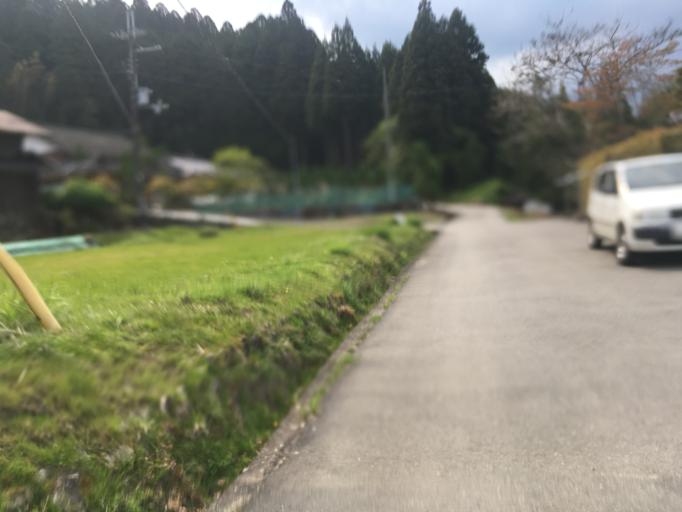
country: JP
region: Kyoto
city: Kameoka
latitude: 35.1354
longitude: 135.6003
